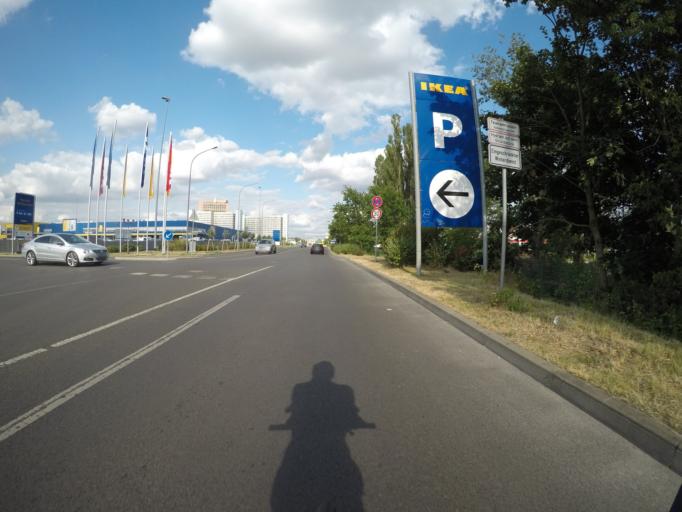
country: DE
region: Berlin
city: Alt-Hohenschoenhausen
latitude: 52.5323
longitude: 13.5115
